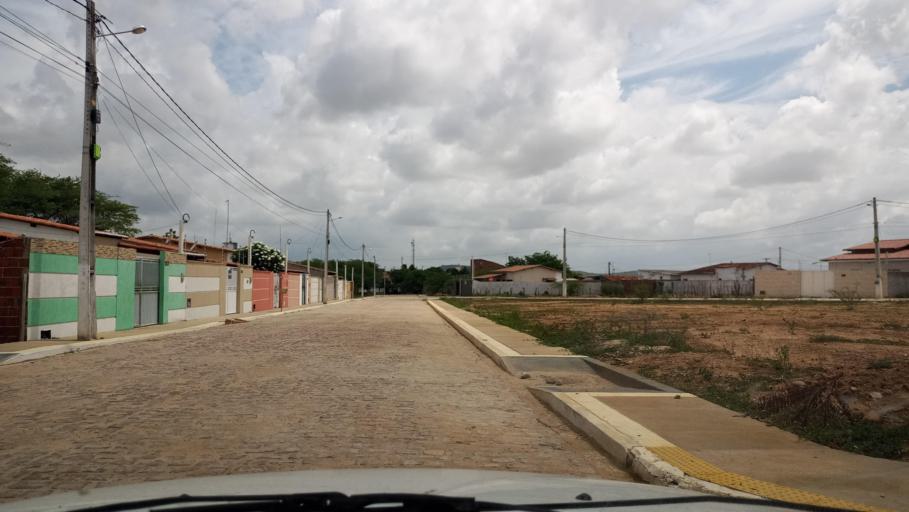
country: BR
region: Rio Grande do Norte
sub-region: Tangara
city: Tangara
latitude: -6.1104
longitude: -35.7158
